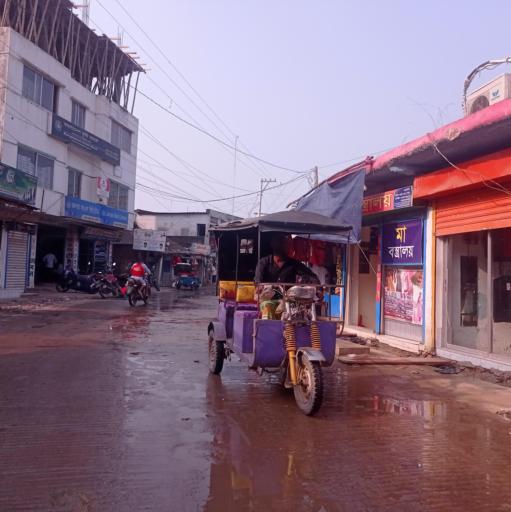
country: BD
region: Dhaka
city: Bhairab Bazar
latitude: 24.1043
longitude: 90.8517
